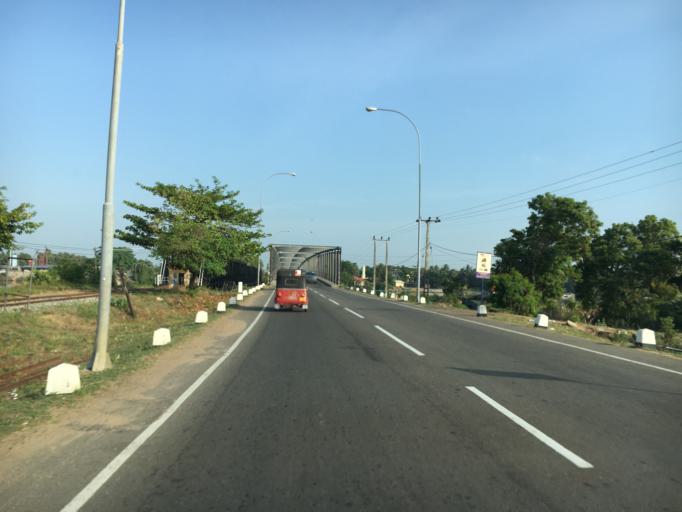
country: LK
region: Eastern Province
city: Eravur Town
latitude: 7.9205
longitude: 81.5163
